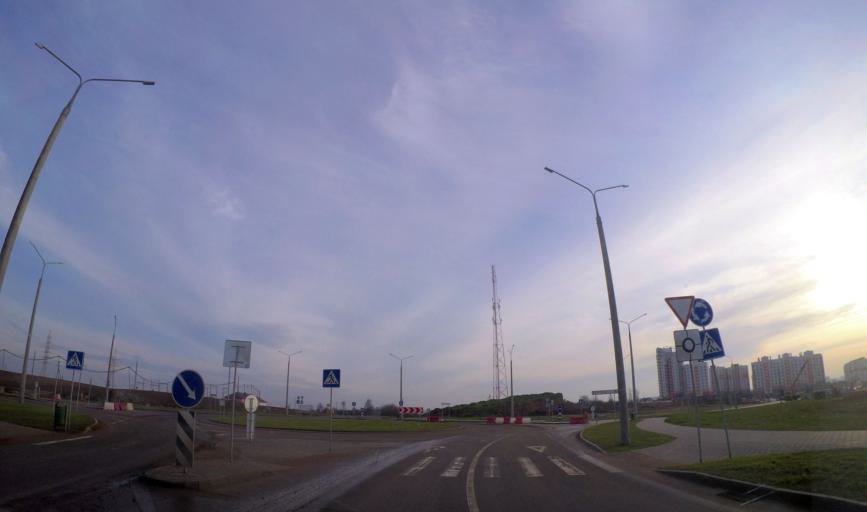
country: BY
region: Grodnenskaya
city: Hrodna
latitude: 53.7164
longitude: 23.8678
